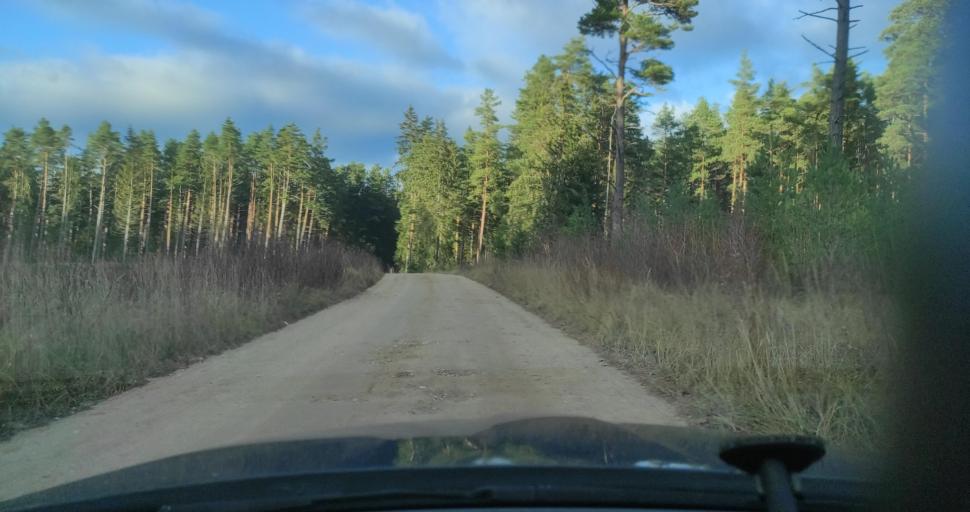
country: LV
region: Kuldigas Rajons
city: Kuldiga
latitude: 57.2823
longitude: 22.0402
